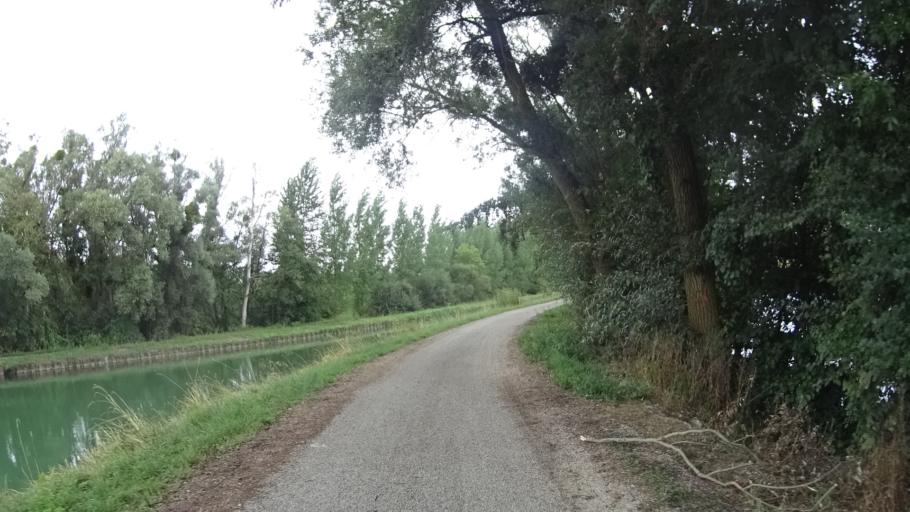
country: FR
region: Picardie
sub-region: Departement de l'Aisne
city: Beautor
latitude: 49.6633
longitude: 3.3506
